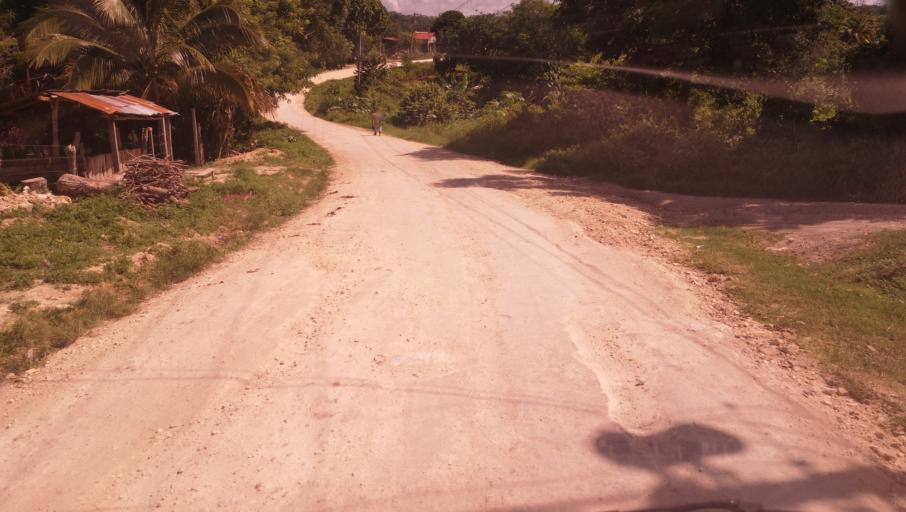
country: GT
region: Peten
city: Melchor de Mencos
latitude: 16.9719
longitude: -89.2649
